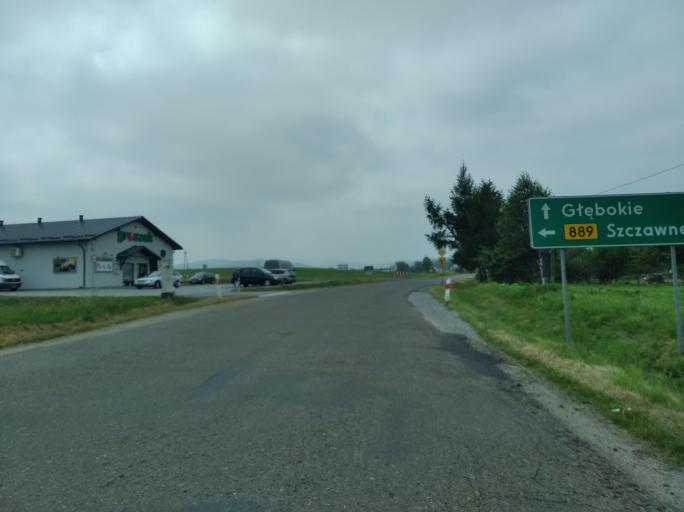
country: PL
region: Subcarpathian Voivodeship
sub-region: Powiat krosnienski
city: Sieniawa
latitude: 49.5655
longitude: 21.9233
